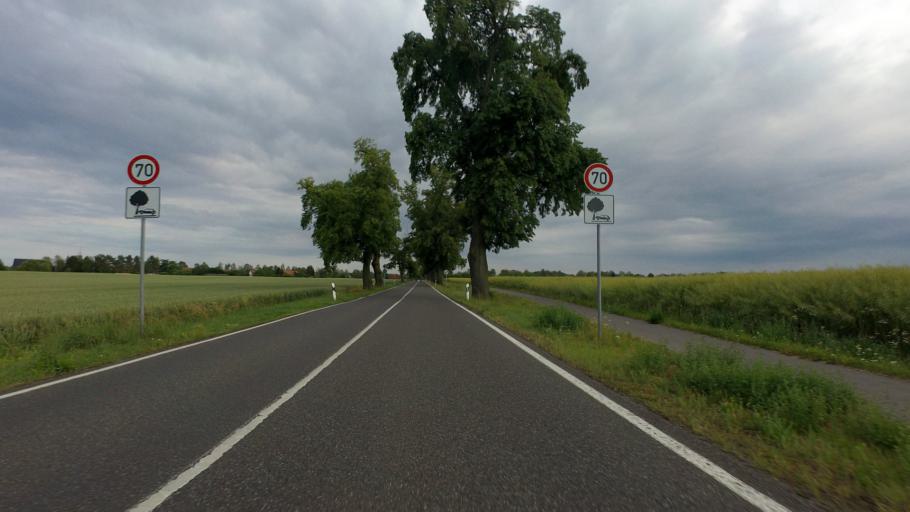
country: DE
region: Brandenburg
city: Pawesin
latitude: 52.5782
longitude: 12.7649
